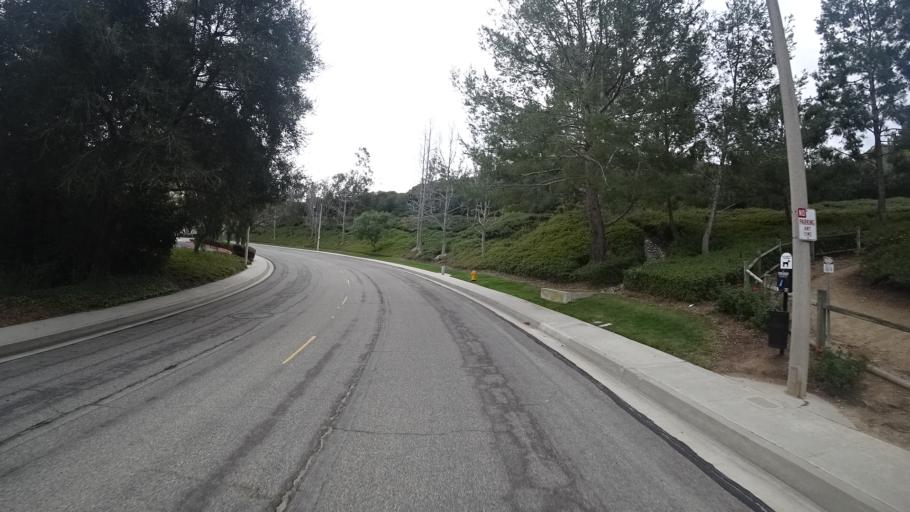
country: US
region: California
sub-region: Orange County
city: Villa Park
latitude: 33.8341
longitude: -117.7731
